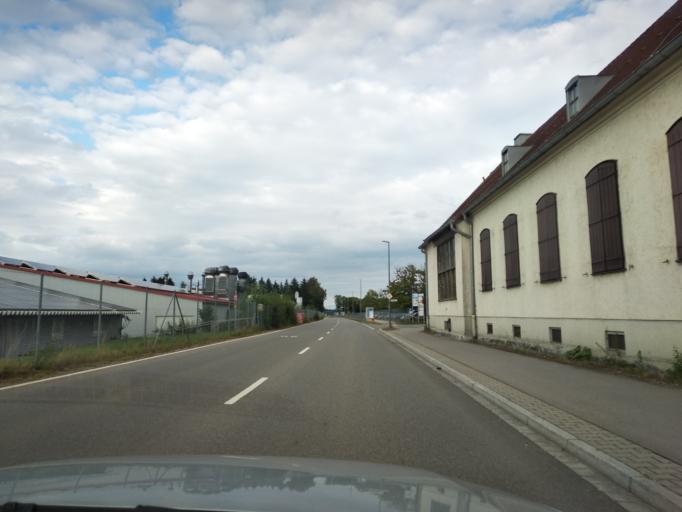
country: DE
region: Bavaria
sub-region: Swabia
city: Memmingerberg
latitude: 47.9909
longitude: 10.2236
